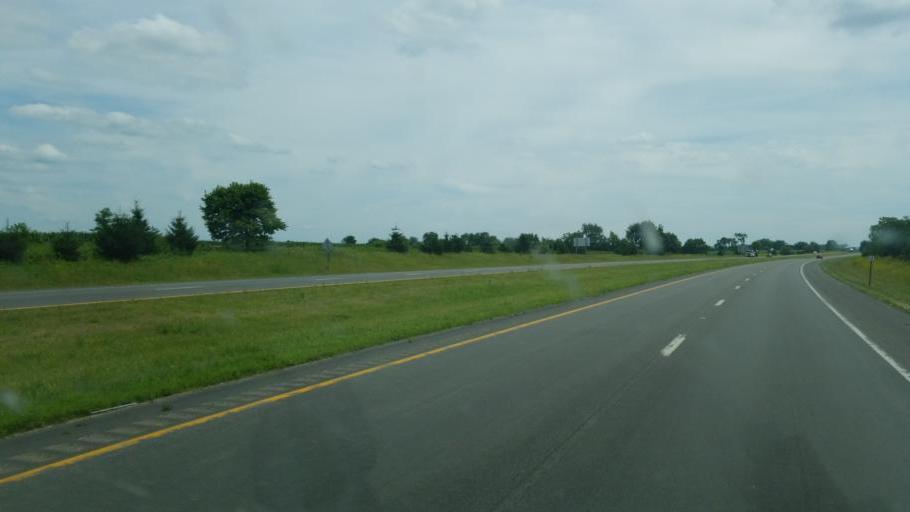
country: US
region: Ohio
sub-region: Knox County
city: Fredericktown
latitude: 40.4665
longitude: -82.5489
